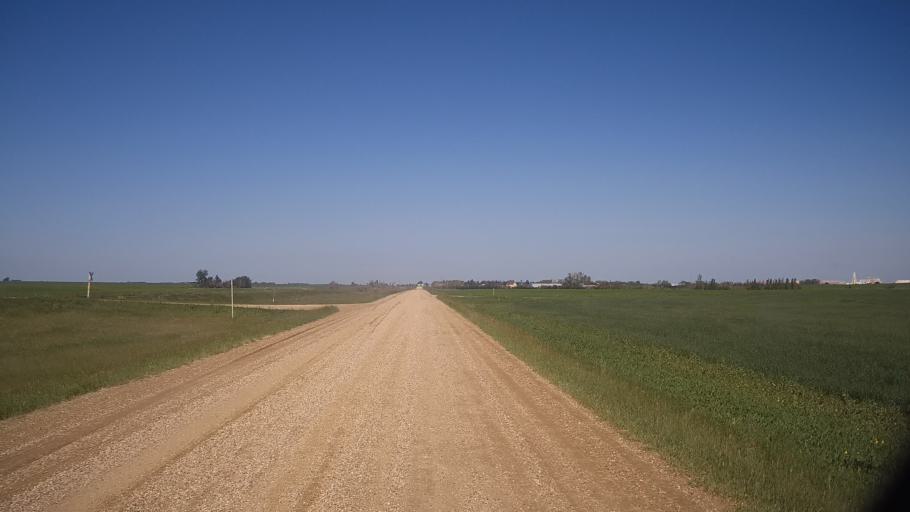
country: CA
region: Saskatchewan
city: Watrous
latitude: 51.8822
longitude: -106.0259
